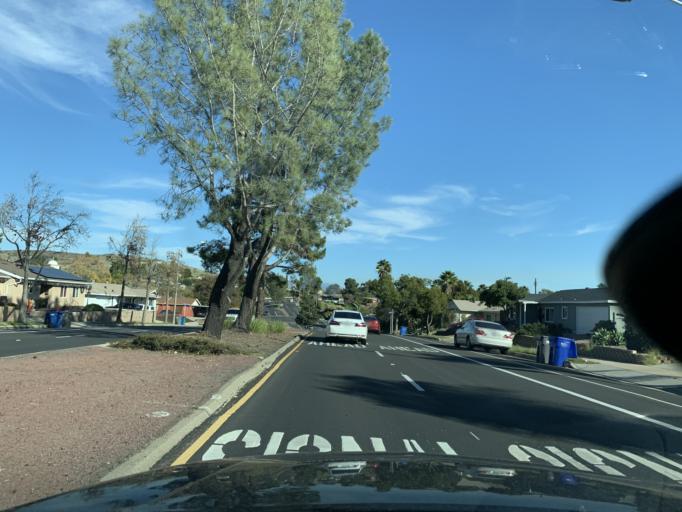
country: US
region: California
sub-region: San Diego County
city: Santee
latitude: 32.8526
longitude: -116.9955
